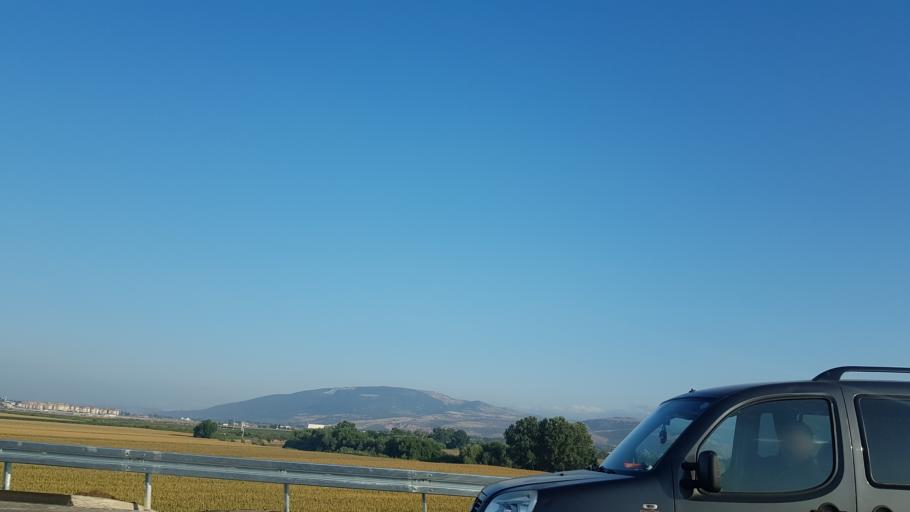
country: TR
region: Bursa
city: Karacabey
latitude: 40.2201
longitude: 28.3995
